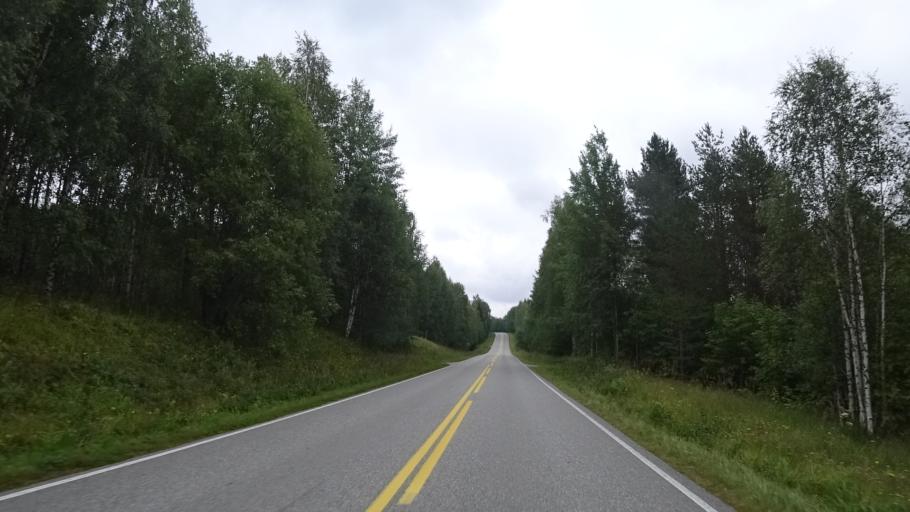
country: FI
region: North Karelia
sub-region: Pielisen Karjala
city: Lieksa
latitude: 63.2809
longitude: 30.5465
